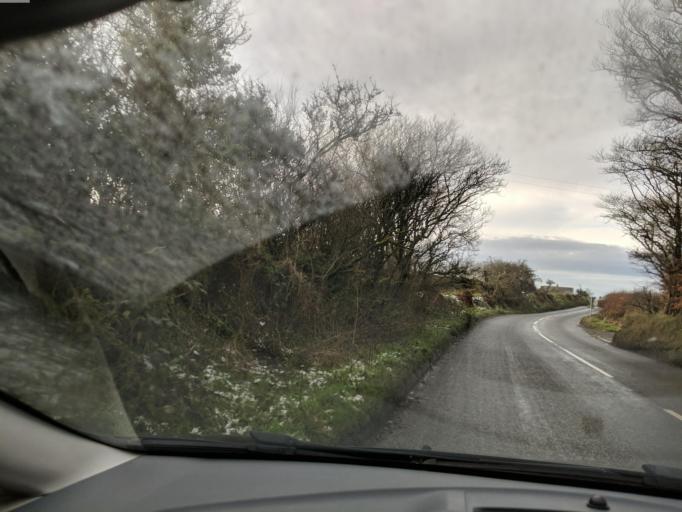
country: GB
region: England
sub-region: Cornwall
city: Jacobstow
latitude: 50.6622
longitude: -4.5782
